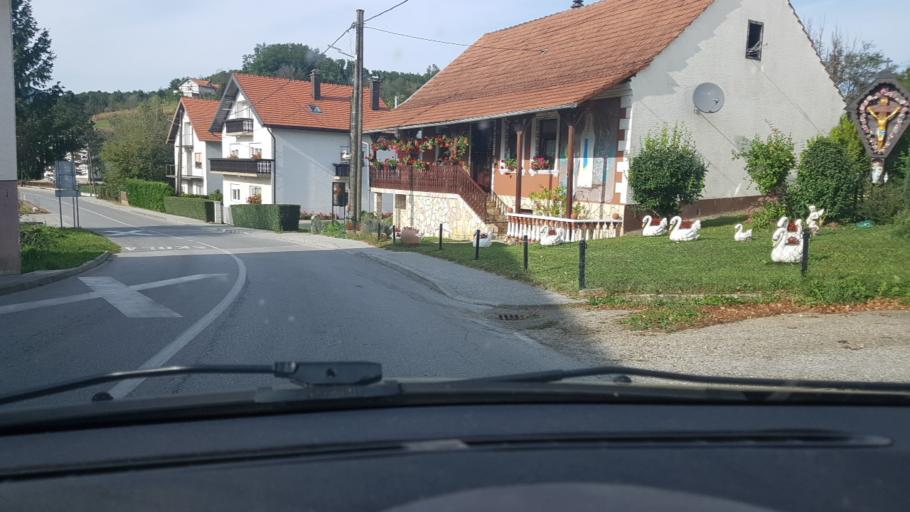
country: HR
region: Krapinsko-Zagorska
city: Mihovljan
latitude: 46.1336
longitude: 15.9699
